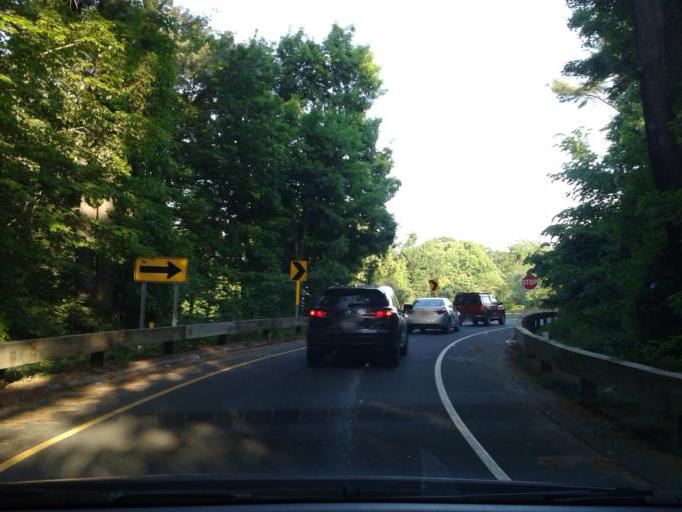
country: US
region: Connecticut
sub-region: Fairfield County
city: North Stamford
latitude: 41.1040
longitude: -73.5657
